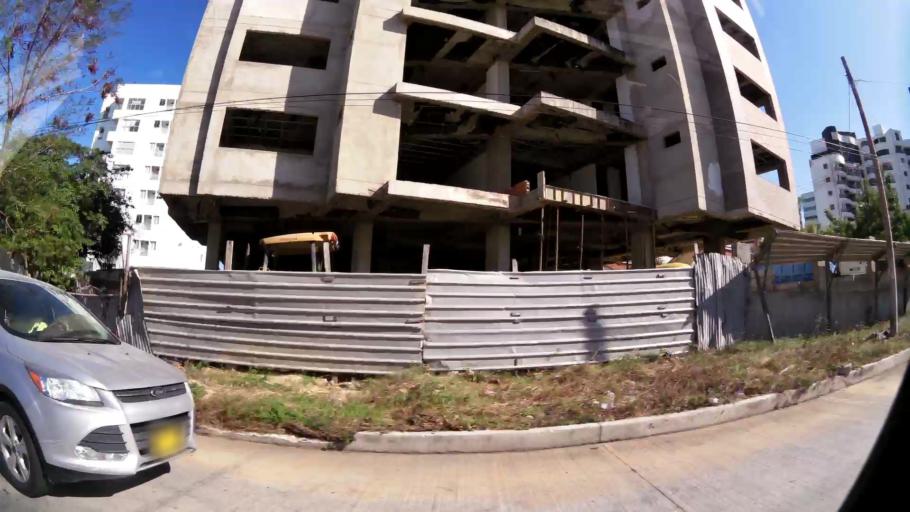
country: CO
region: Atlantico
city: Barranquilla
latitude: 11.0190
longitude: -74.8225
